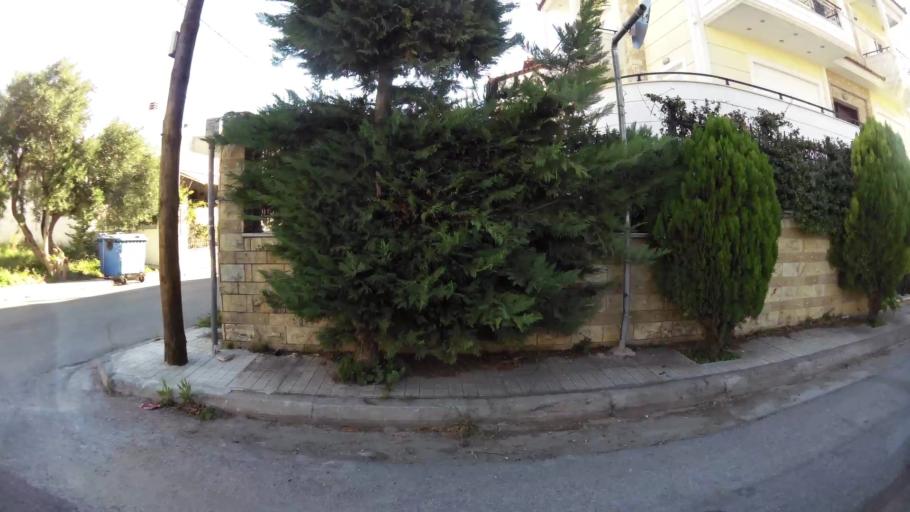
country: GR
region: Attica
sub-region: Nomarchia Anatolikis Attikis
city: Gerakas
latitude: 38.0110
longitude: 23.8490
